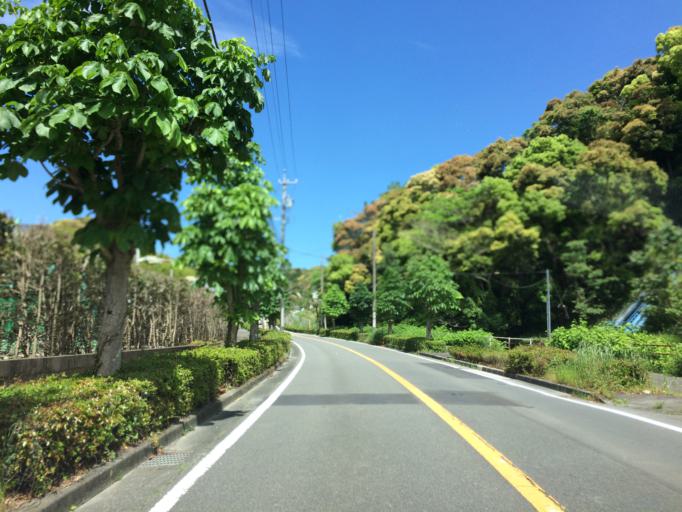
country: JP
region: Shizuoka
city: Fujieda
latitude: 34.8543
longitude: 138.2325
